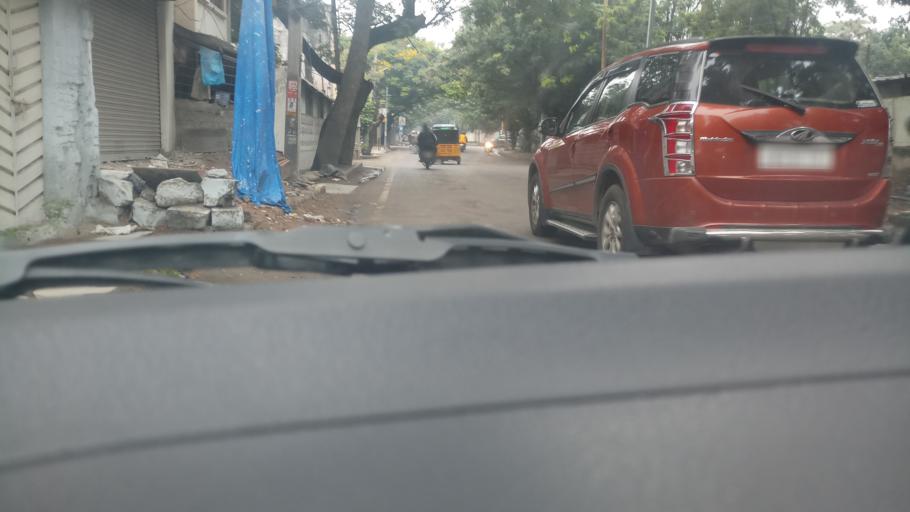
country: IN
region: Telangana
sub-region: Hyderabad
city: Hyderabad
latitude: 17.3968
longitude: 78.4545
